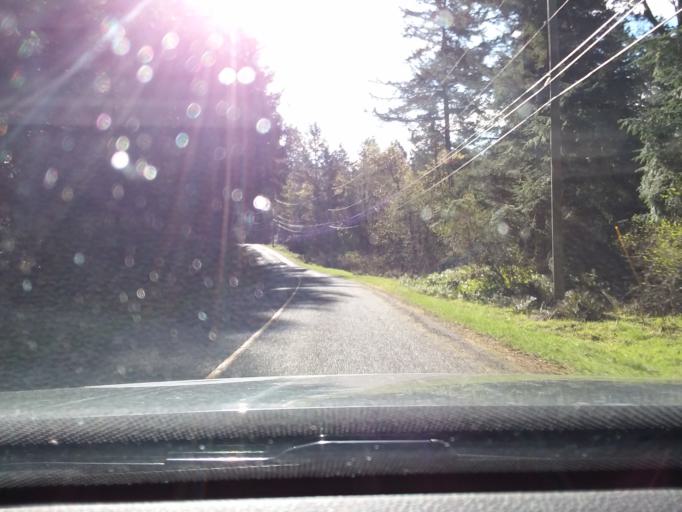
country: CA
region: British Columbia
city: North Cowichan
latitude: 48.9505
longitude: -123.5279
